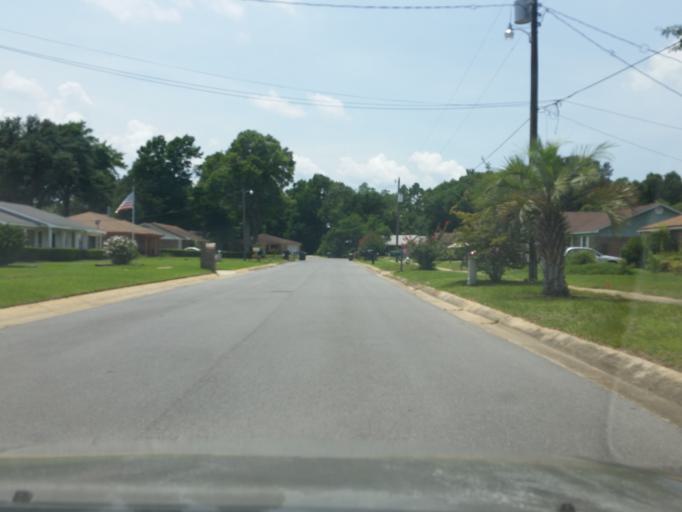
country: US
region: Florida
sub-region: Escambia County
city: Ferry Pass
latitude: 30.5190
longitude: -87.1855
